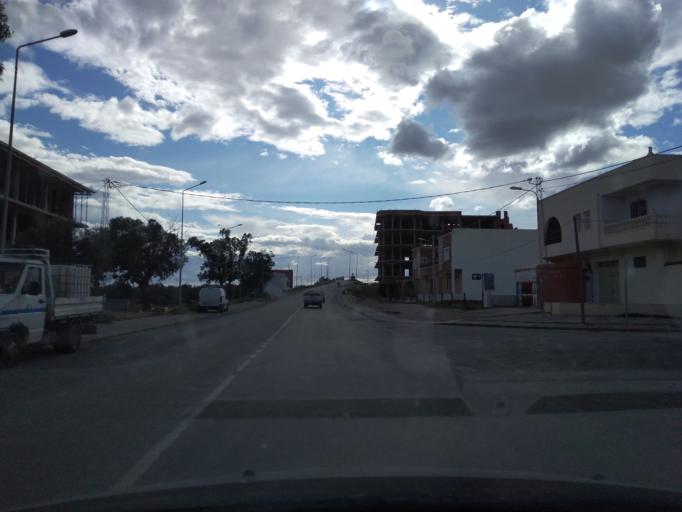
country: TN
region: Susah
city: Masakin
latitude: 35.7139
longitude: 10.5613
